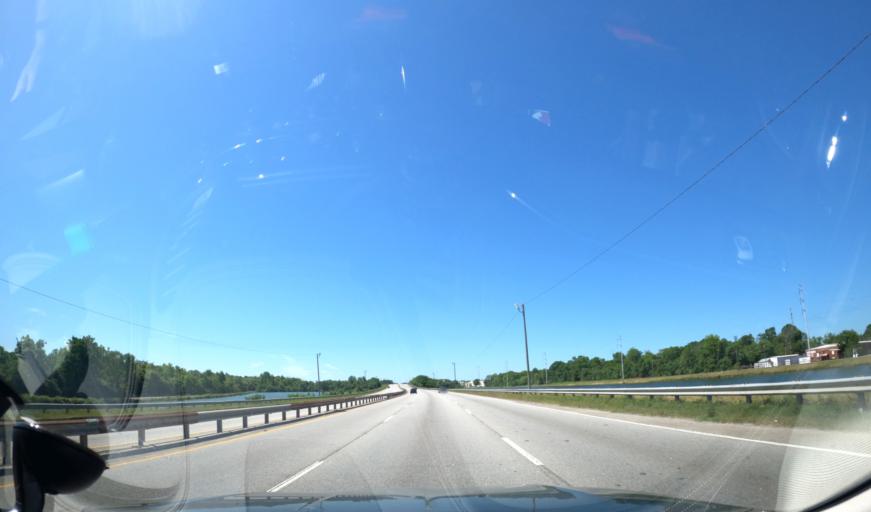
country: US
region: Georgia
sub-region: Richmond County
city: Augusta
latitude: 33.4516
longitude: -81.9732
